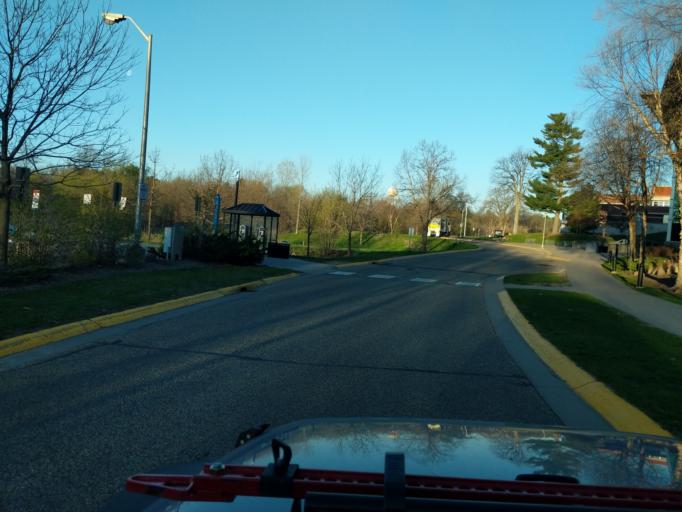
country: US
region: Wisconsin
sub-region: Pierce County
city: River Falls
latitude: 44.8522
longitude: -92.6203
